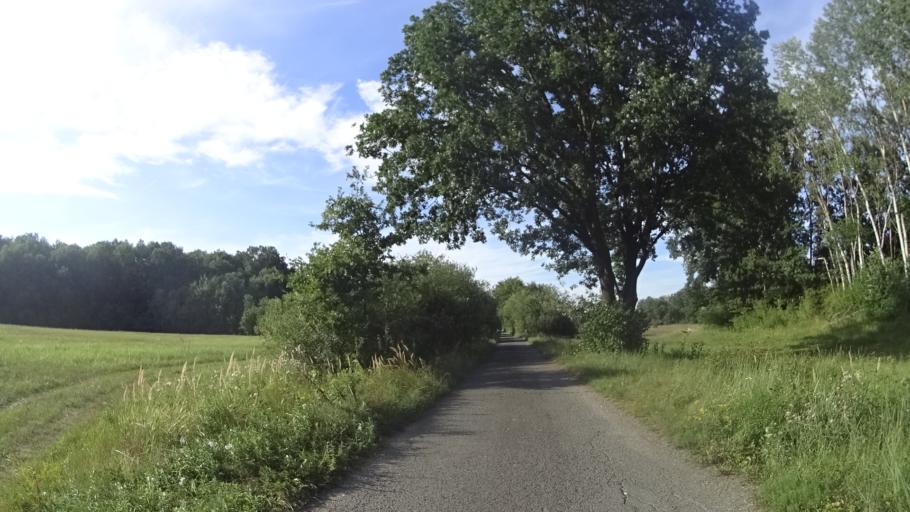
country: AT
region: Lower Austria
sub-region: Politischer Bezirk Mistelbach
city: Rabensburg
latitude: 48.6006
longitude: 16.9497
